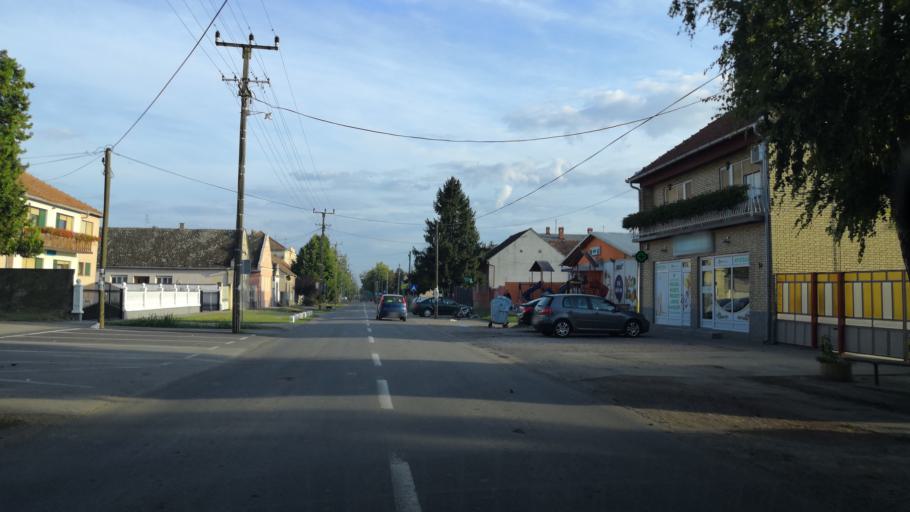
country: RS
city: Novi Karlovci
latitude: 45.0800
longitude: 20.1779
